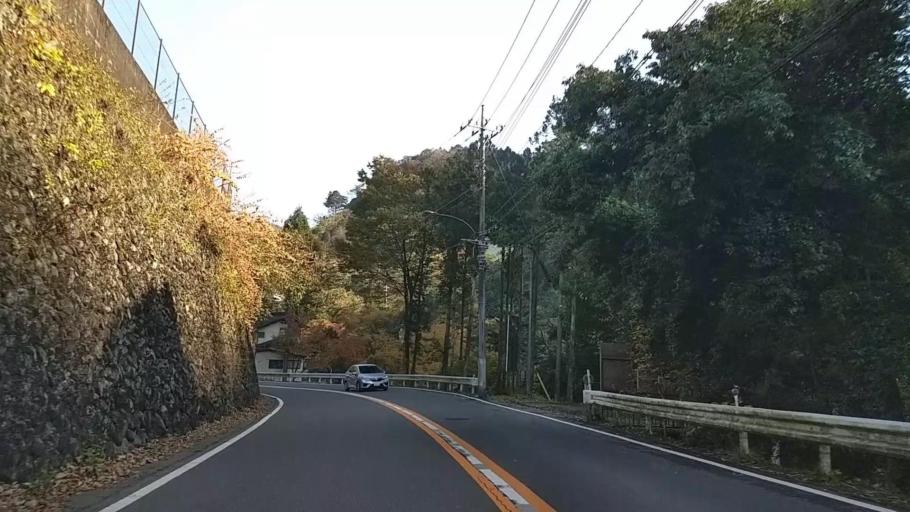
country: JP
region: Tokyo
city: Itsukaichi
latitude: 35.8022
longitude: 139.1050
